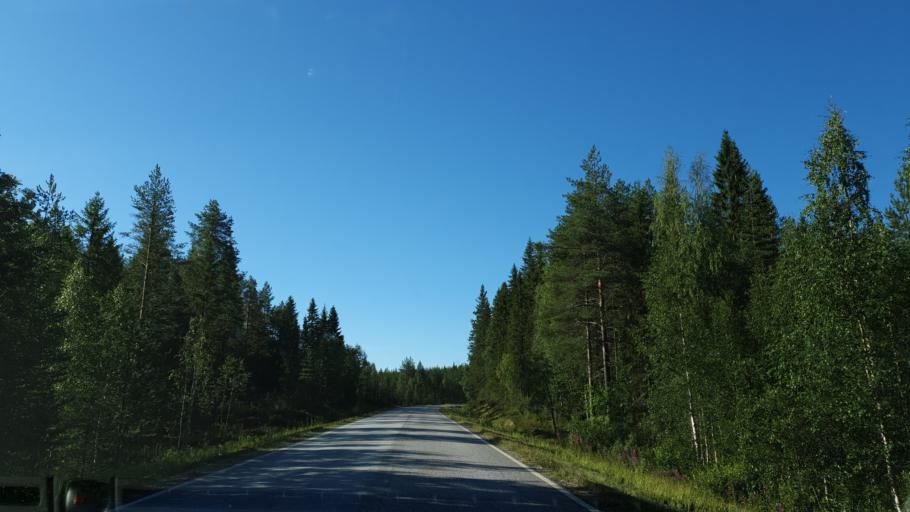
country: FI
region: Kainuu
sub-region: Kehys-Kainuu
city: Kuhmo
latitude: 64.3554
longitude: 29.4896
